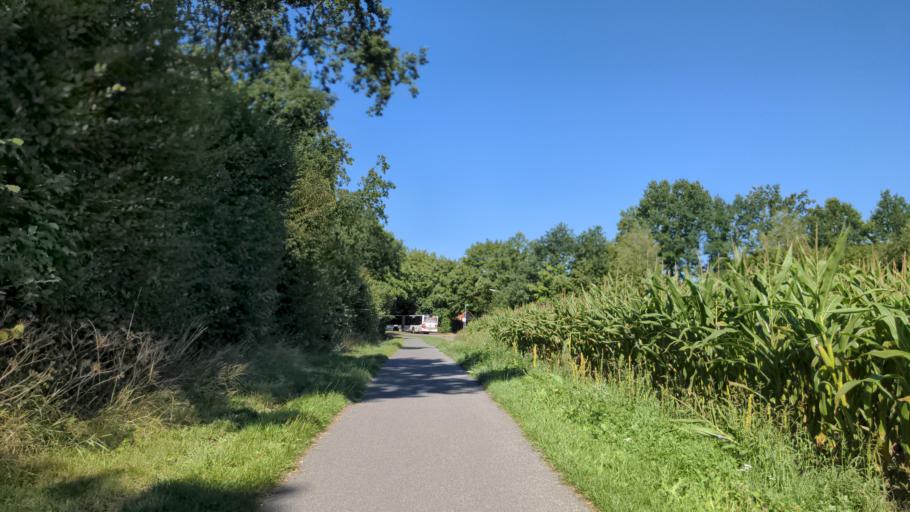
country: DE
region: Schleswig-Holstein
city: Krummesse
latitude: 53.7743
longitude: 10.6551
